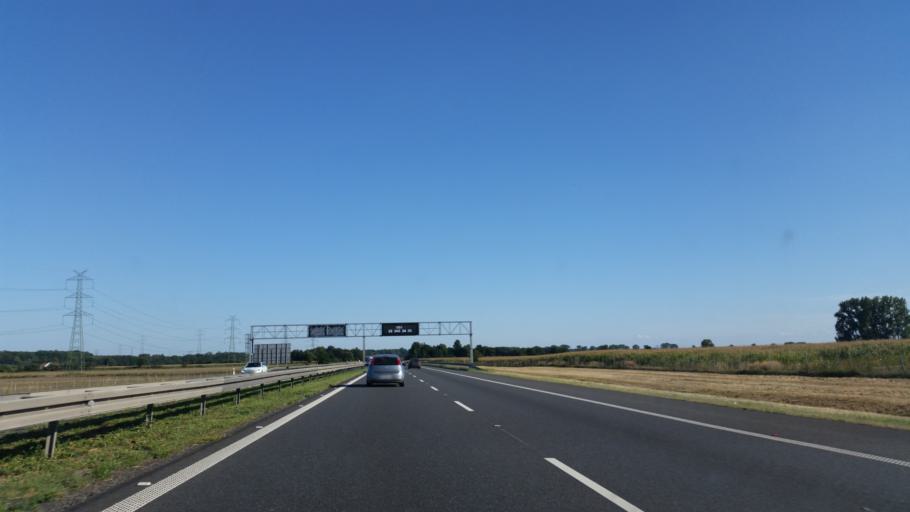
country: PL
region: Lower Silesian Voivodeship
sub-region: Powiat strzelinski
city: Wiazow
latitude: 50.8644
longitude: 17.2194
